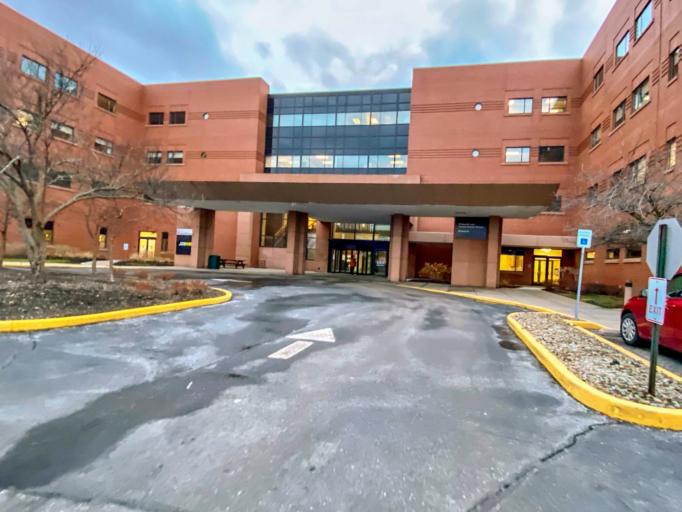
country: US
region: Ohio
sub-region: Summit County
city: Akron
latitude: 41.0821
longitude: -81.4988
